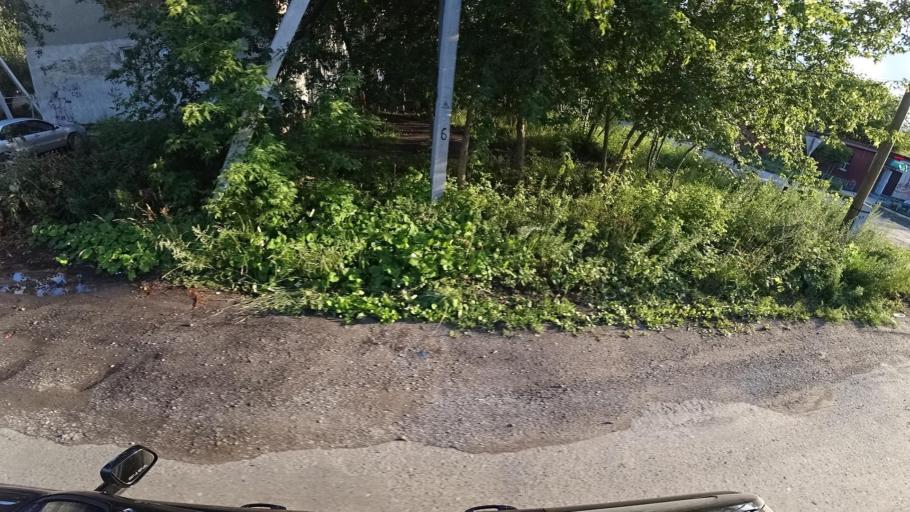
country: RU
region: Sverdlovsk
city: Kamyshlov
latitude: 56.8508
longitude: 62.7271
